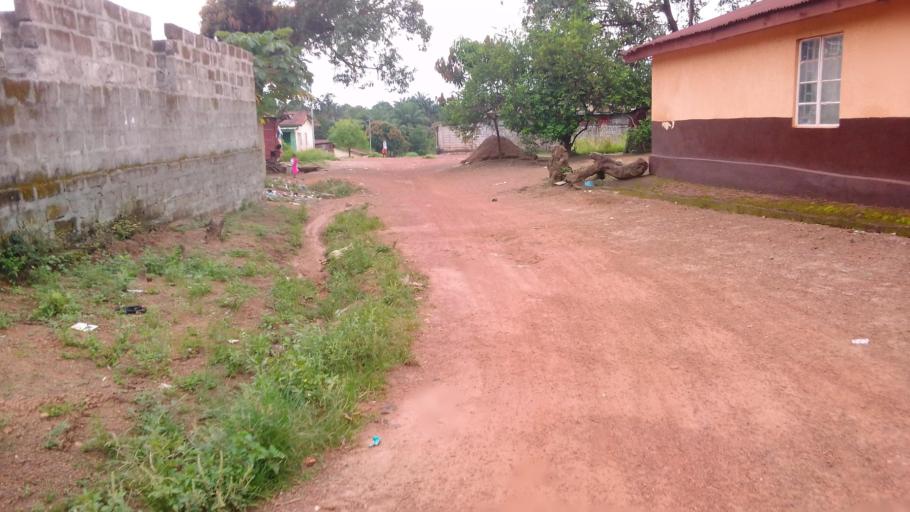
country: SL
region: Northern Province
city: Makeni
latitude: 8.8808
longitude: -12.0428
